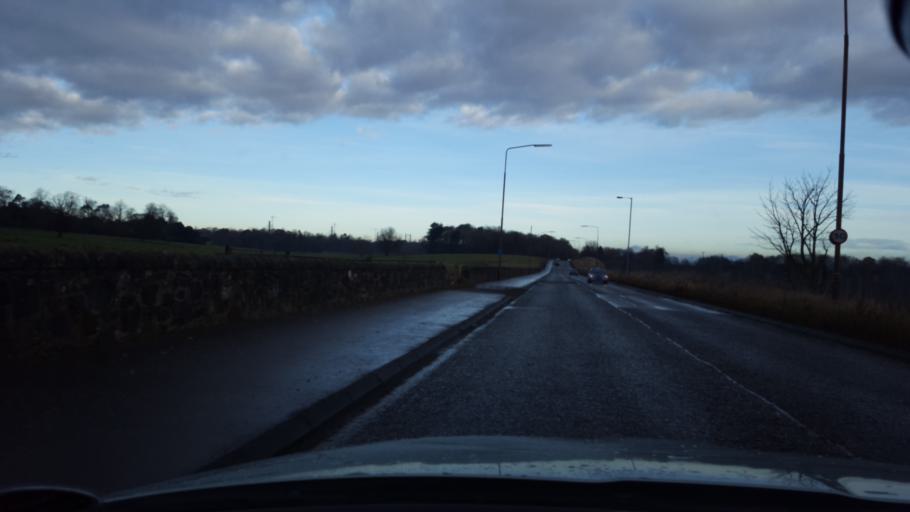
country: GB
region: Scotland
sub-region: Edinburgh
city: Kirkliston
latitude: 55.9678
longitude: -3.4014
